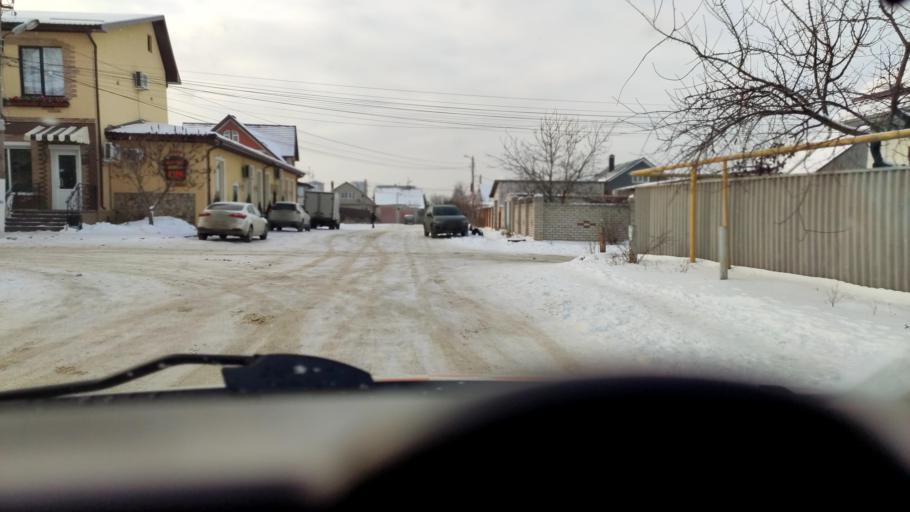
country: RU
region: Voronezj
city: Podgornoye
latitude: 51.7263
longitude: 39.1565
